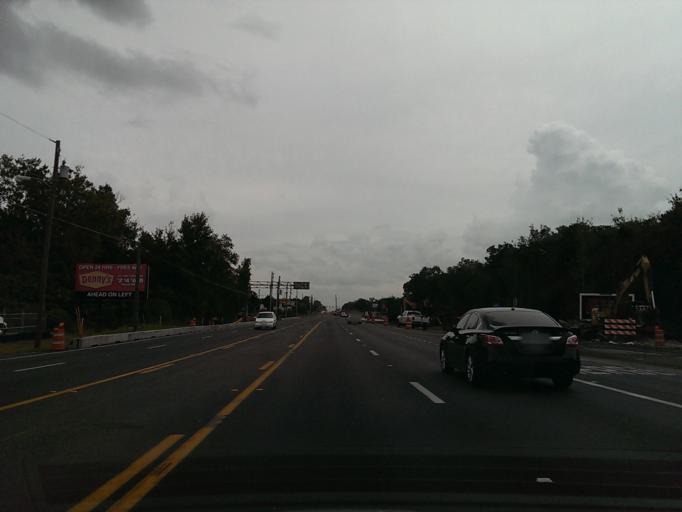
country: US
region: Florida
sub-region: Orange County
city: Ocoee
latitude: 28.5516
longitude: -81.5494
